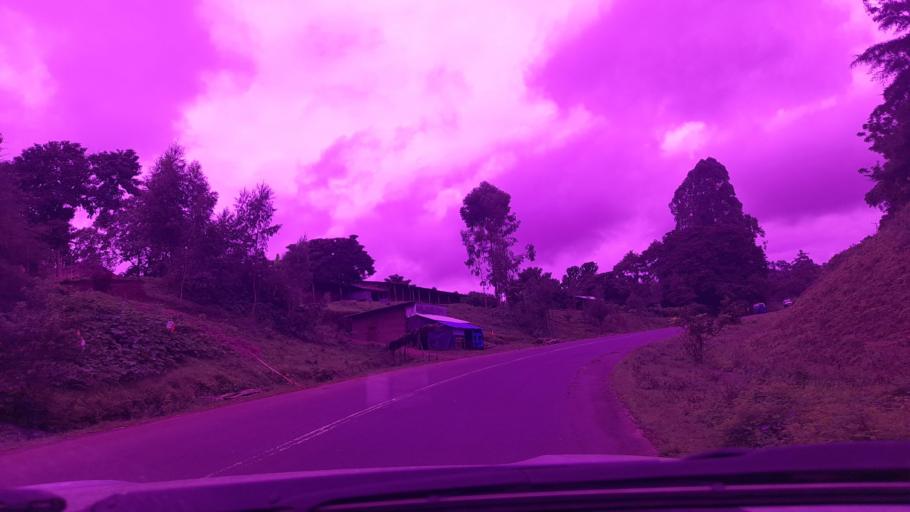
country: ET
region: Southern Nations, Nationalities, and People's Region
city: Bonga
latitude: 7.2825
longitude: 35.9702
